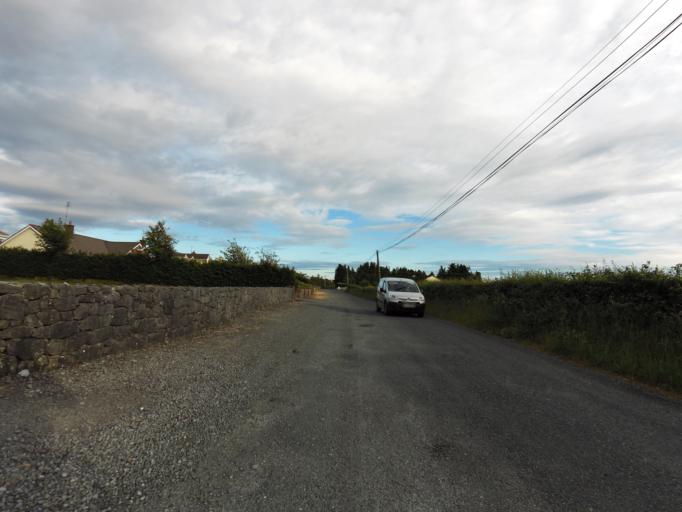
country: IE
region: Connaught
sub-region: County Galway
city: Athenry
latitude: 53.2971
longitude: -8.7346
